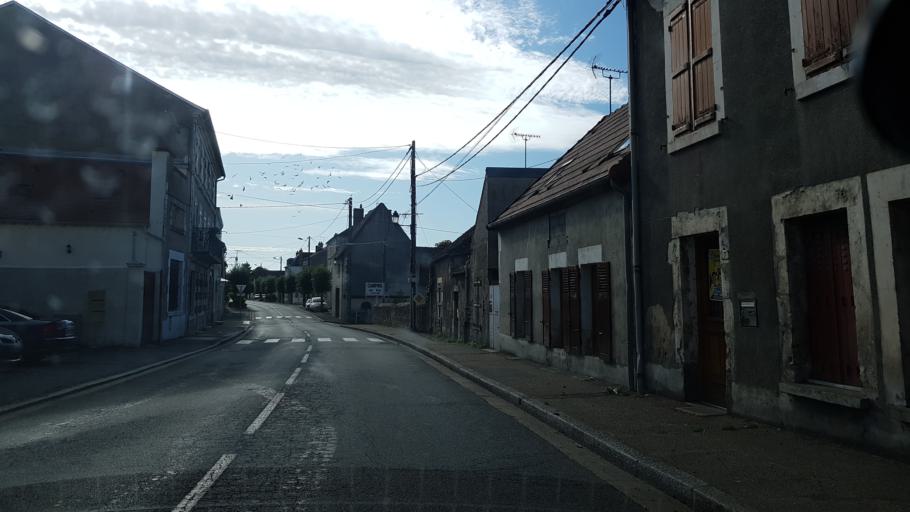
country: FR
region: Centre
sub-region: Departement du Loiret
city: Bonny-sur-Loire
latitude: 47.5592
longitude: 2.8403
